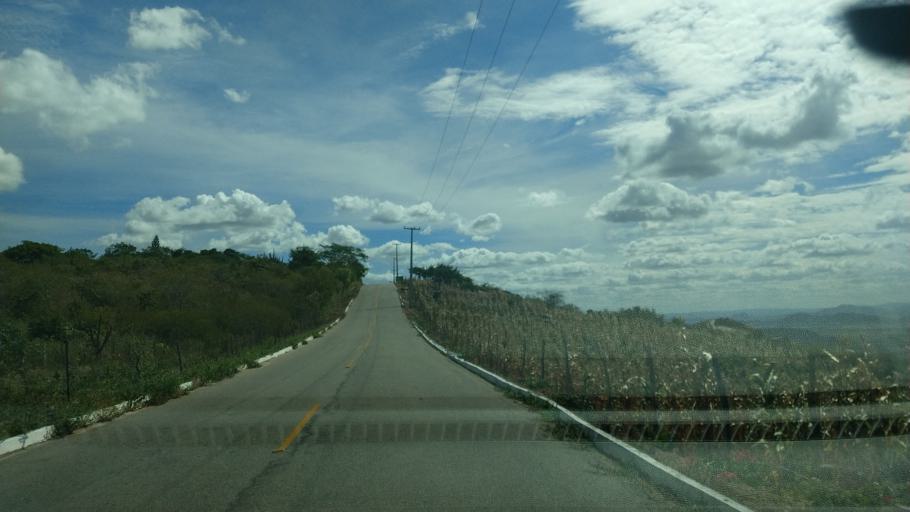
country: BR
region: Rio Grande do Norte
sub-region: Sao Jose Do Campestre
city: Sao Jose do Campestre
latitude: -6.4197
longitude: -35.7601
